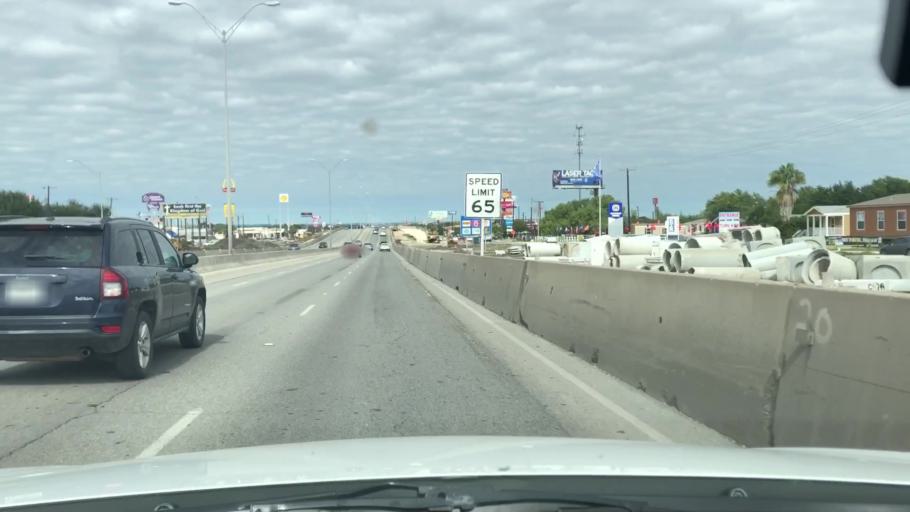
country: US
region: Texas
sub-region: Bexar County
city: Lackland Air Force Base
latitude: 29.4135
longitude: -98.6495
